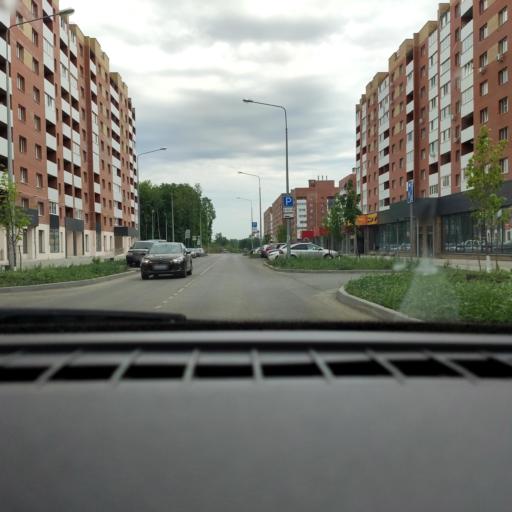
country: RU
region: Samara
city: Petra-Dubrava
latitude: 53.3067
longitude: 50.2850
